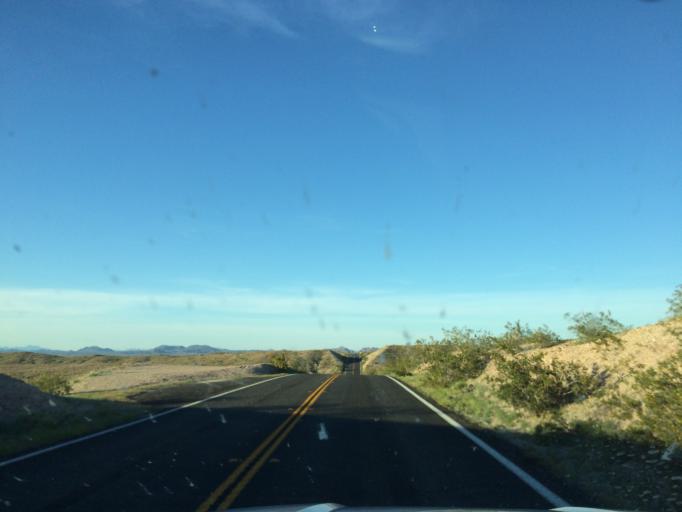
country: US
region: California
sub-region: Riverside County
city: Mesa Verde
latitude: 33.1945
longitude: -114.8597
